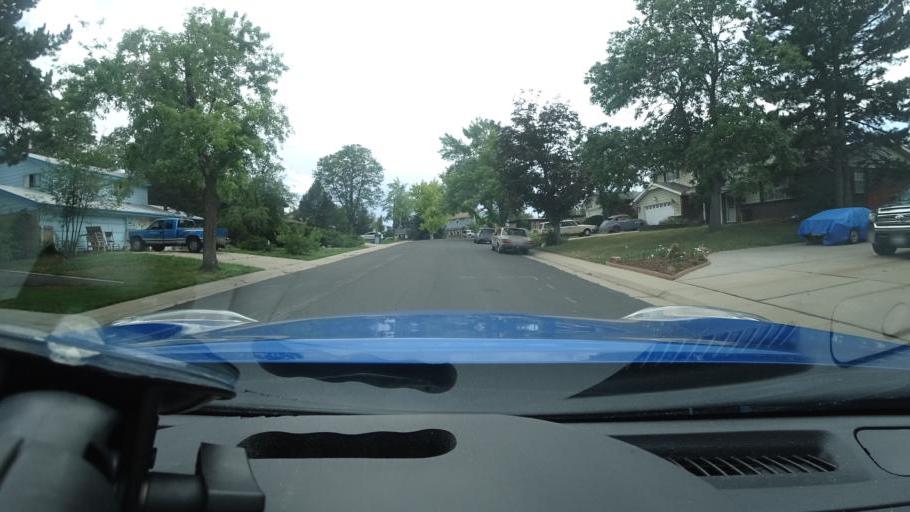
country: US
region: Colorado
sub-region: Adams County
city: Aurora
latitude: 39.7214
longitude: -104.8343
